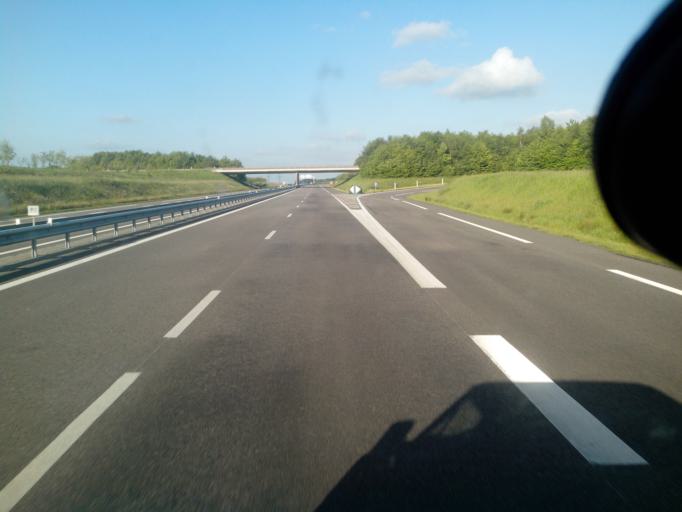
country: FR
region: Haute-Normandie
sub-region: Departement de la Seine-Maritime
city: Totes
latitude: 49.6376
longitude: 1.0499
